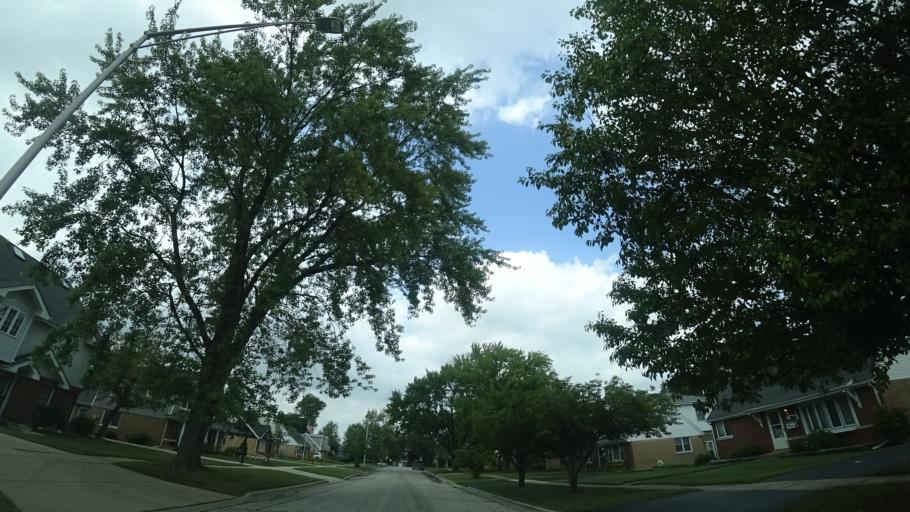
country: US
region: Illinois
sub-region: Cook County
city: Oak Lawn
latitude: 41.6930
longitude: -87.7609
